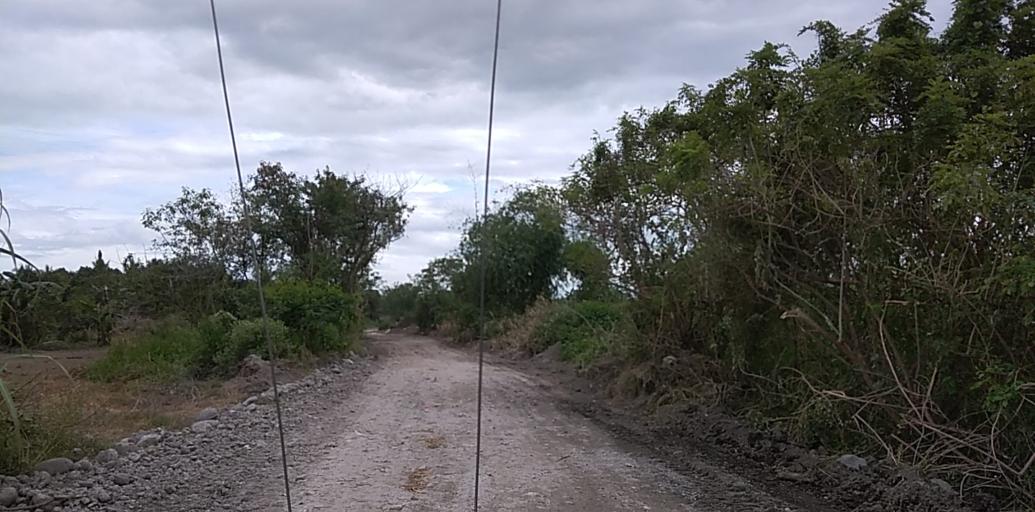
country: PH
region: Central Luzon
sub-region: Province of Pampanga
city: Pulung Santol
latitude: 15.0409
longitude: 120.5575
